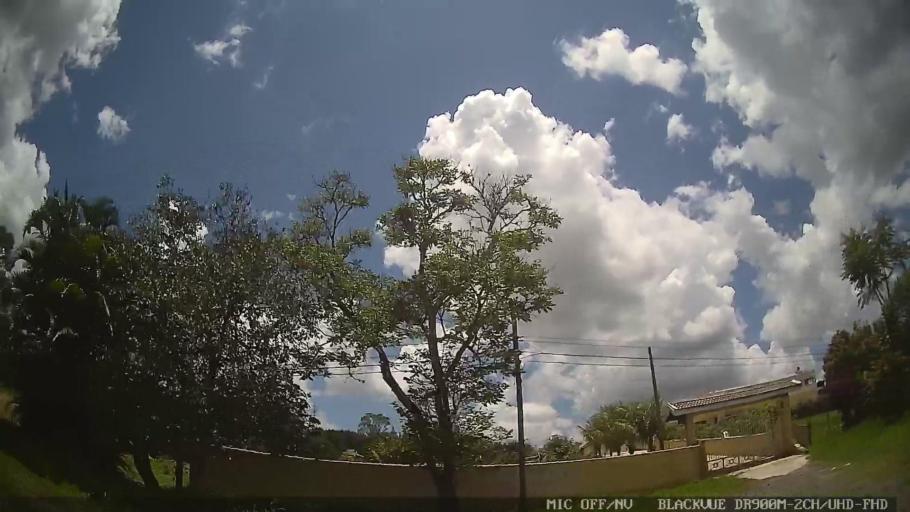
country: BR
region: Sao Paulo
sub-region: Serra Negra
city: Serra Negra
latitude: -22.6359
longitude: -46.7282
